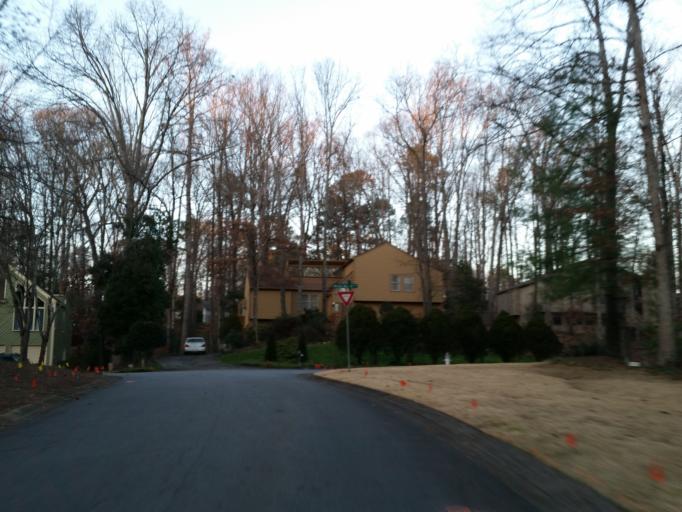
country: US
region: Georgia
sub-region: Fulton County
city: Sandy Springs
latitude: 33.9625
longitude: -84.3990
